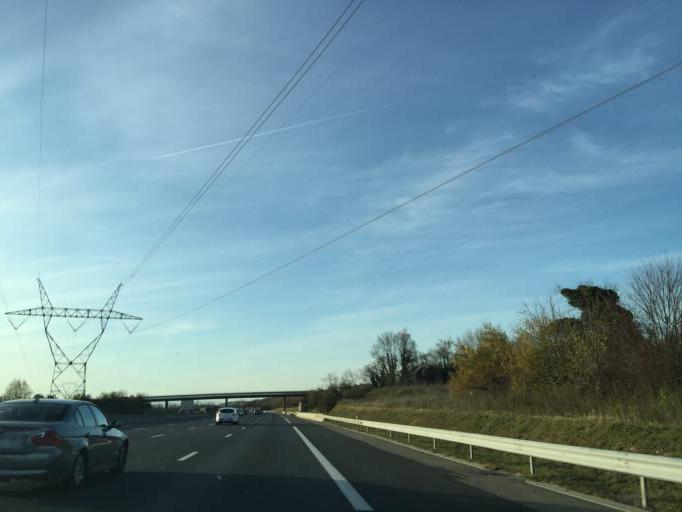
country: FR
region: Rhone-Alpes
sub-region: Departement du Rhone
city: Saint-Laurent-de-Mure
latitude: 45.6775
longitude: 5.0299
